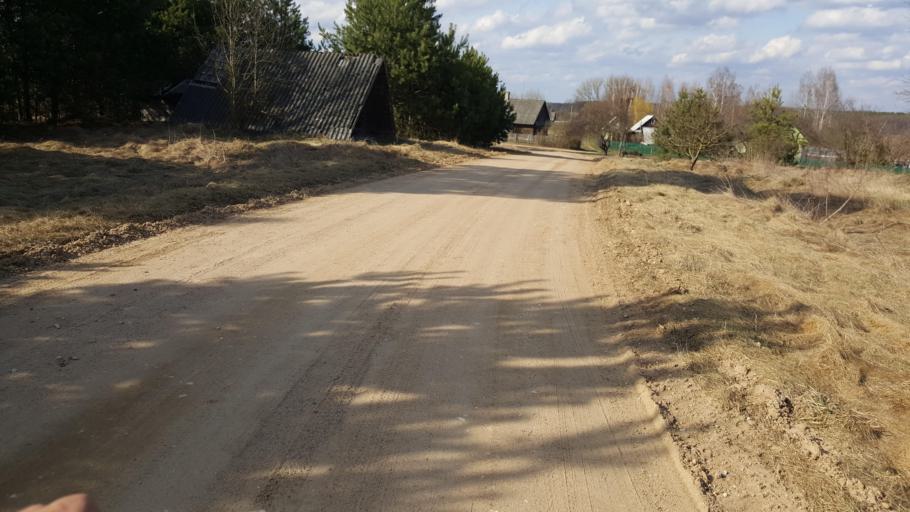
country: BY
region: Brest
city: Kamyanyets
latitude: 52.4141
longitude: 23.9318
